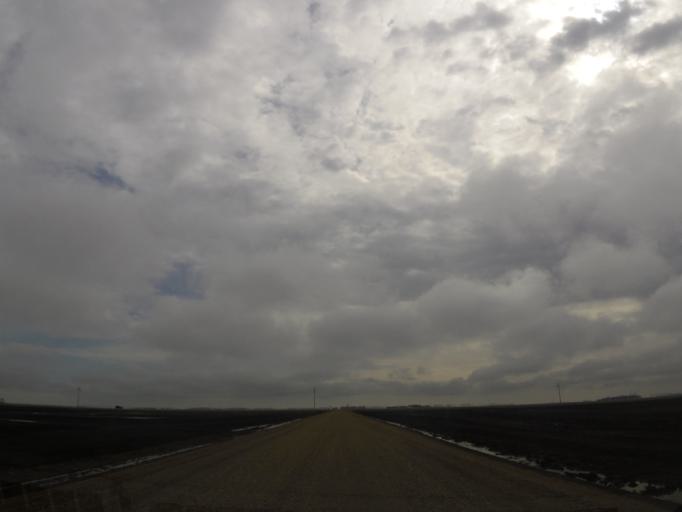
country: US
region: North Dakota
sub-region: Walsh County
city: Grafton
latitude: 48.4152
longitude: -97.3212
